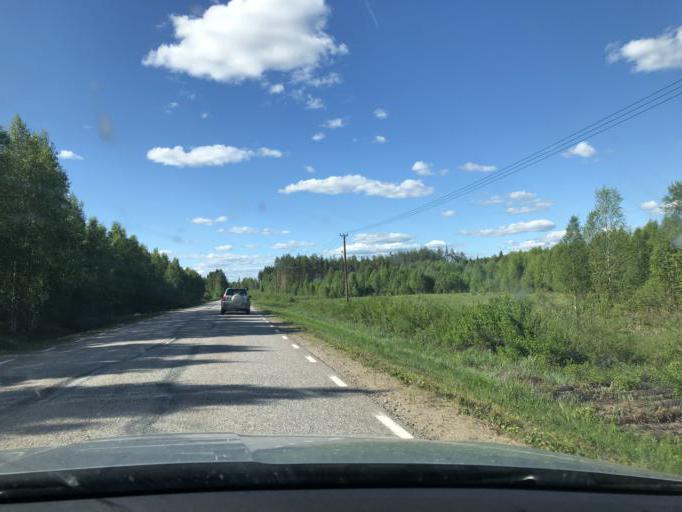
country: SE
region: Norrbotten
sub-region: Kalix Kommun
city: Kalix
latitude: 65.9377
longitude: 23.1589
